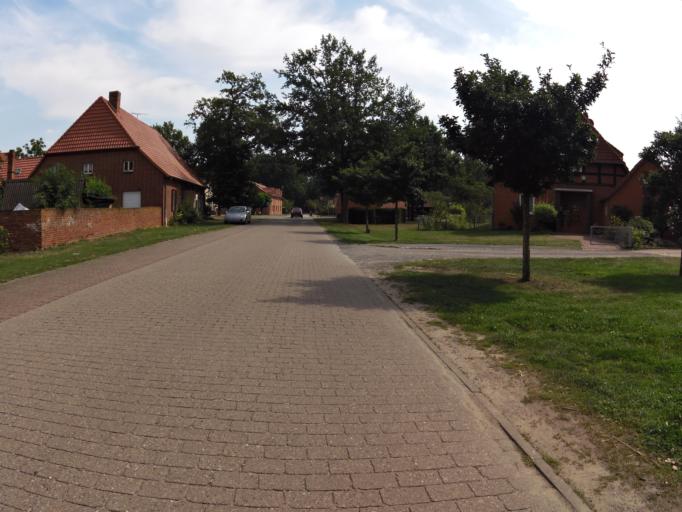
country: DE
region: Lower Saxony
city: Estorf
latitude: 52.5887
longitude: 9.1406
